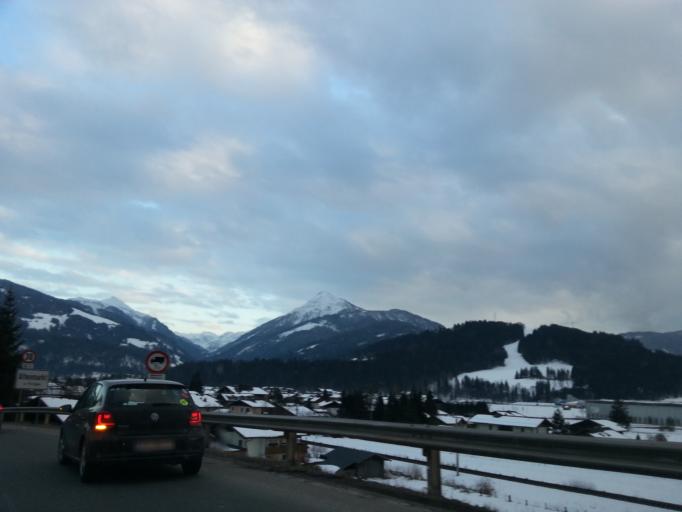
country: AT
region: Salzburg
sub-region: Politischer Bezirk Sankt Johann im Pongau
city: Altenmarkt im Pongau
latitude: 47.3888
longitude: 13.4116
